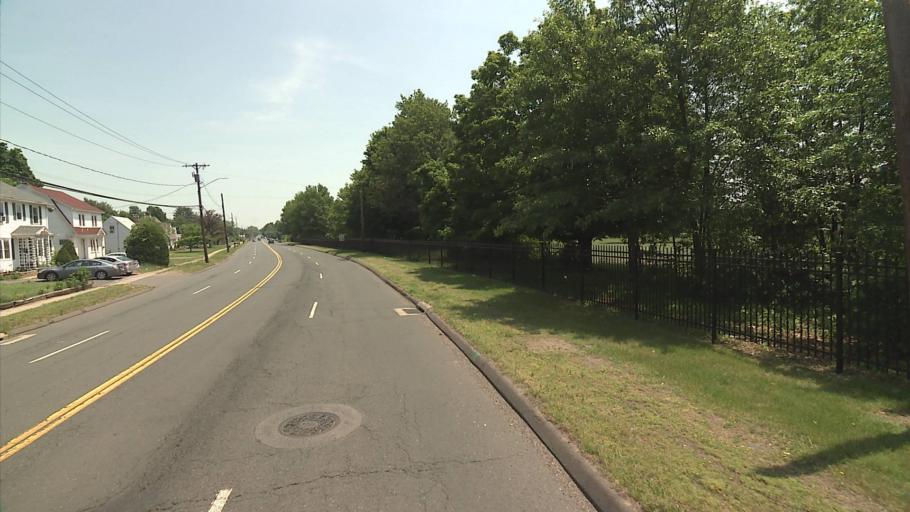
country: US
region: Connecticut
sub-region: Hartford County
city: East Hartford
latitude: 41.7626
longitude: -72.6225
